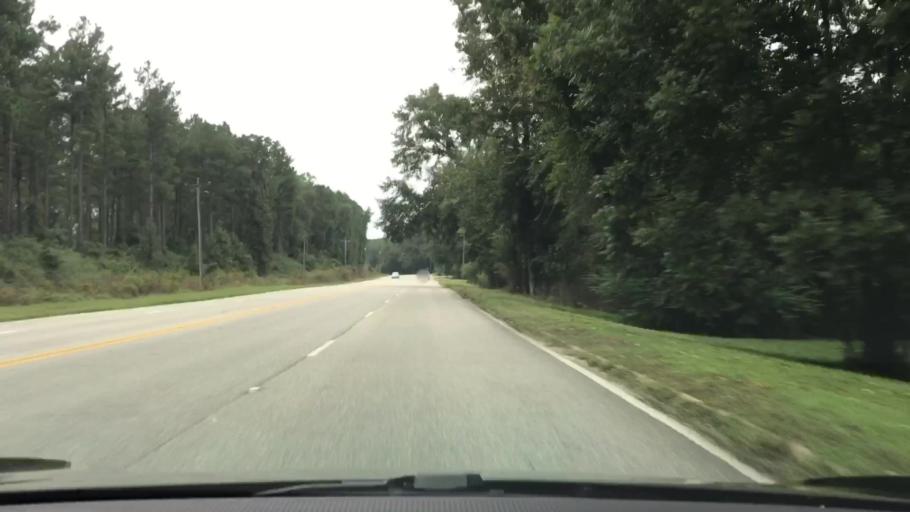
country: US
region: Alabama
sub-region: Coffee County
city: Elba
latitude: 31.4503
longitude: -86.0704
